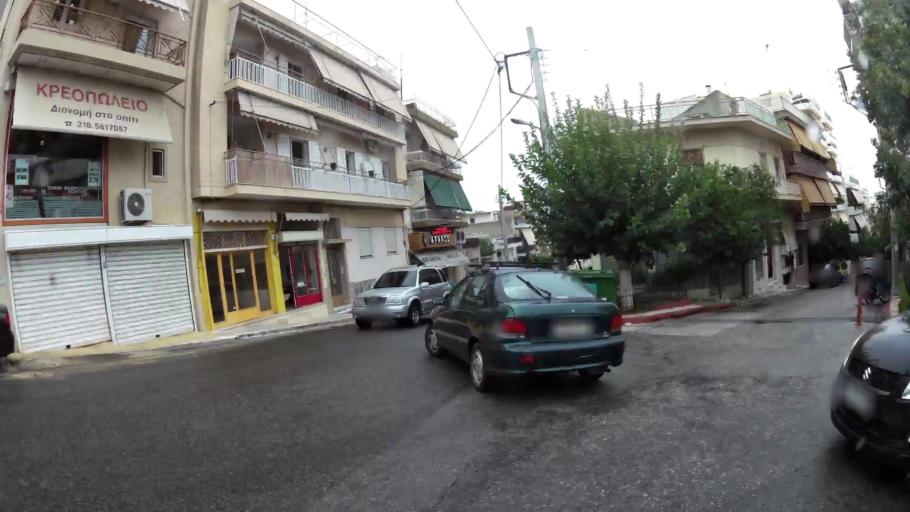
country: GR
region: Attica
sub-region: Nomarchia Athinas
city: Agia Varvara
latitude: 37.9910
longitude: 23.6526
